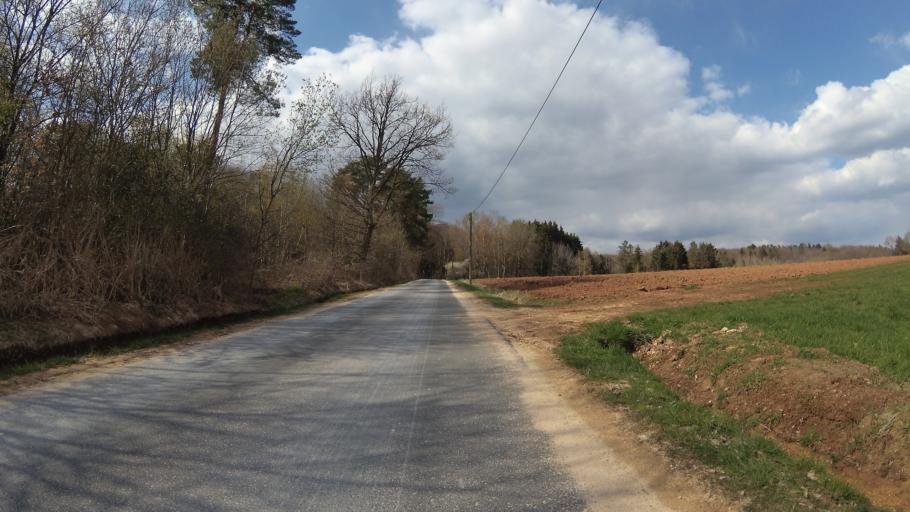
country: DE
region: Saarland
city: Oberthal
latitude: 49.5268
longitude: 7.1068
